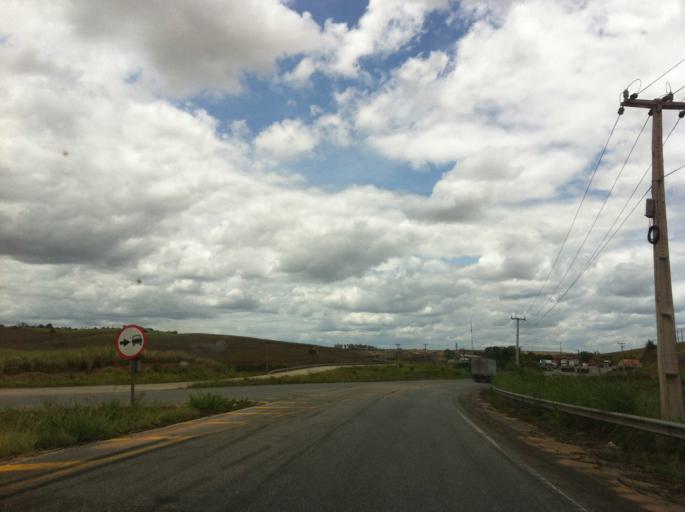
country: BR
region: Alagoas
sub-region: Novo Lino
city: Novo Lino
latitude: -8.8865
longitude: -35.6321
